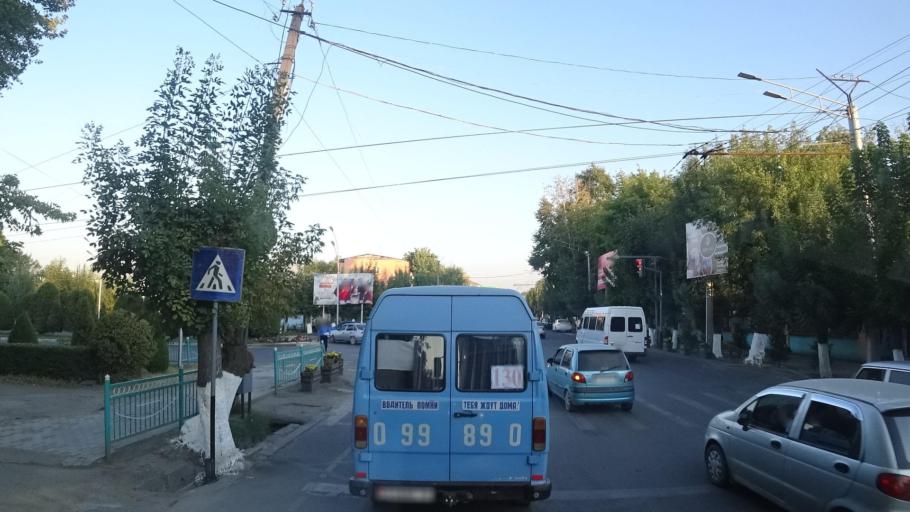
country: KG
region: Osh
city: Osh
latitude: 40.5250
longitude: 72.7969
